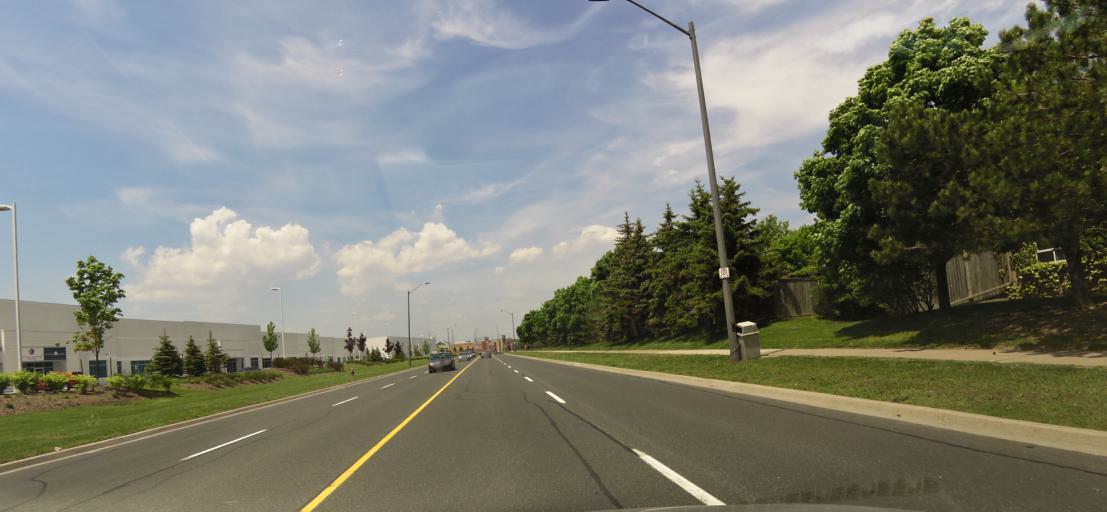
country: CA
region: Ontario
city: Mississauga
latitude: 43.5246
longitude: -79.7083
